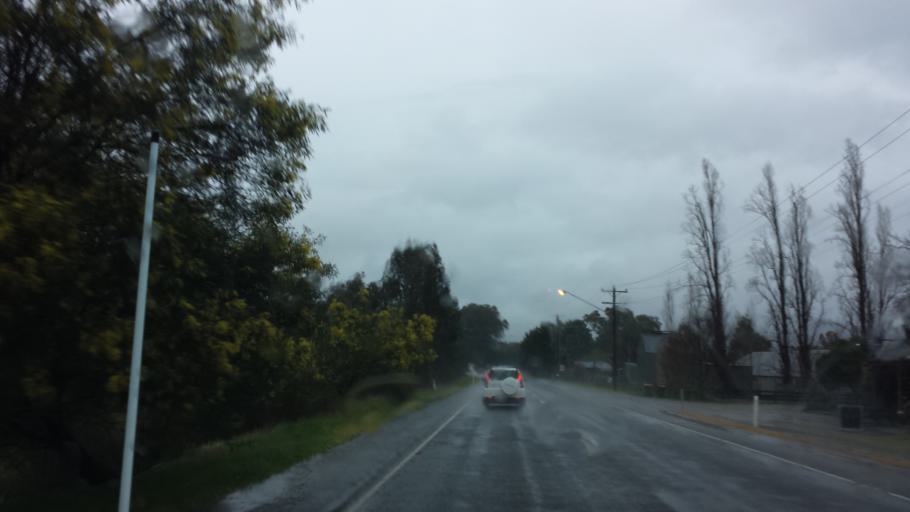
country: AU
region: Victoria
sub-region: Alpine
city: Mount Beauty
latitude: -36.5862
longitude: 146.7589
